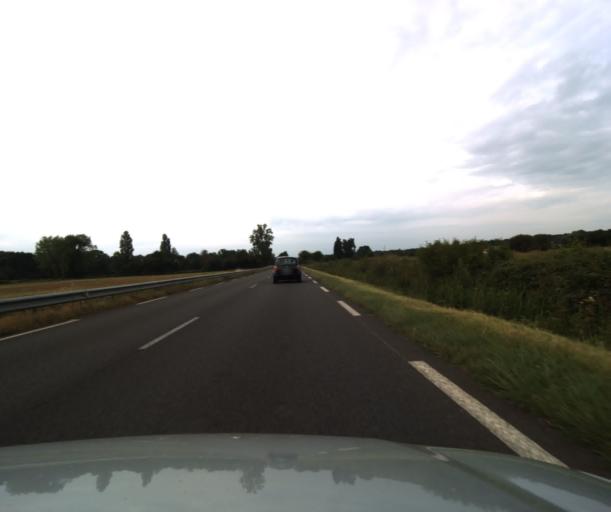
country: FR
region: Midi-Pyrenees
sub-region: Departement des Hautes-Pyrenees
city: Rabastens-de-Bigorre
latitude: 43.3449
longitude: 0.1346
